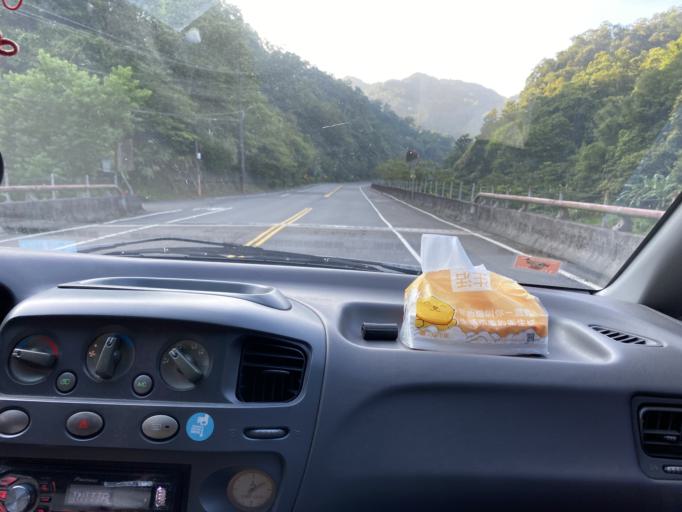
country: TW
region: Taiwan
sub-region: Keelung
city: Keelung
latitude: 25.0300
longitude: 121.7795
